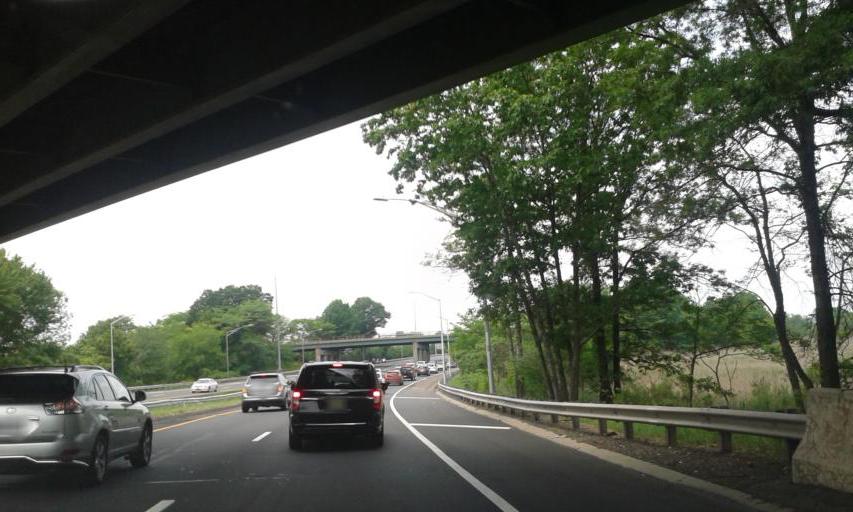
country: US
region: New York
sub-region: Richmond County
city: Bloomfield
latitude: 40.6219
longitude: -74.1730
